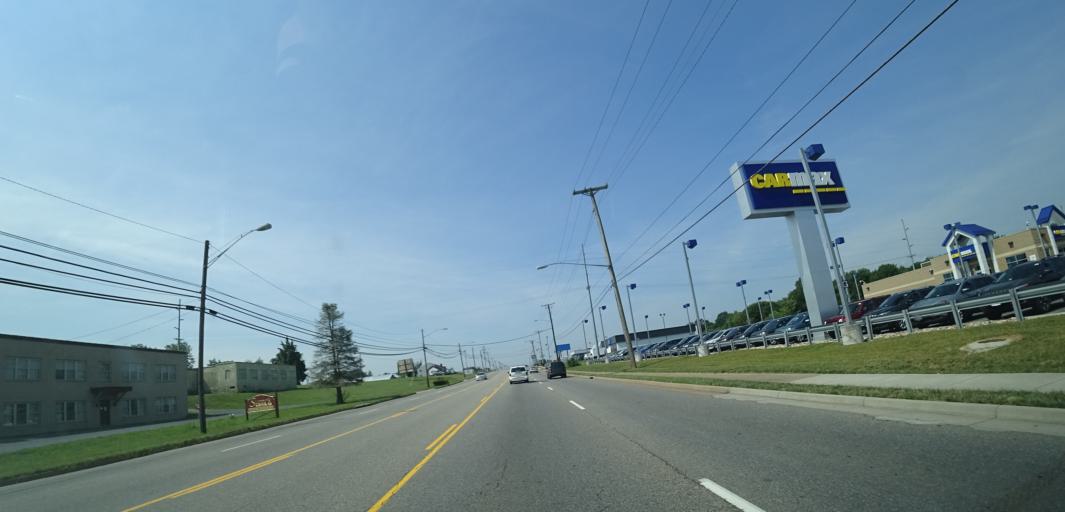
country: US
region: Virginia
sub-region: City of Harrisonburg
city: Harrisonburg
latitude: 38.4184
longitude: -78.8957
